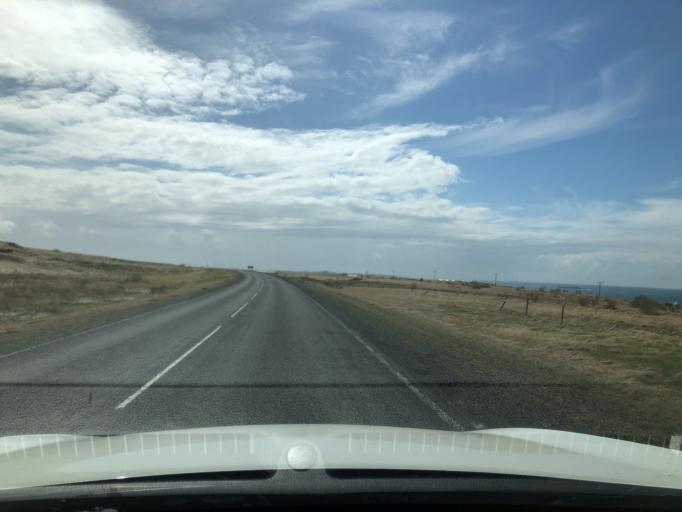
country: IS
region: Capital Region
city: Reykjavik
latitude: 64.2801
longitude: -21.8333
